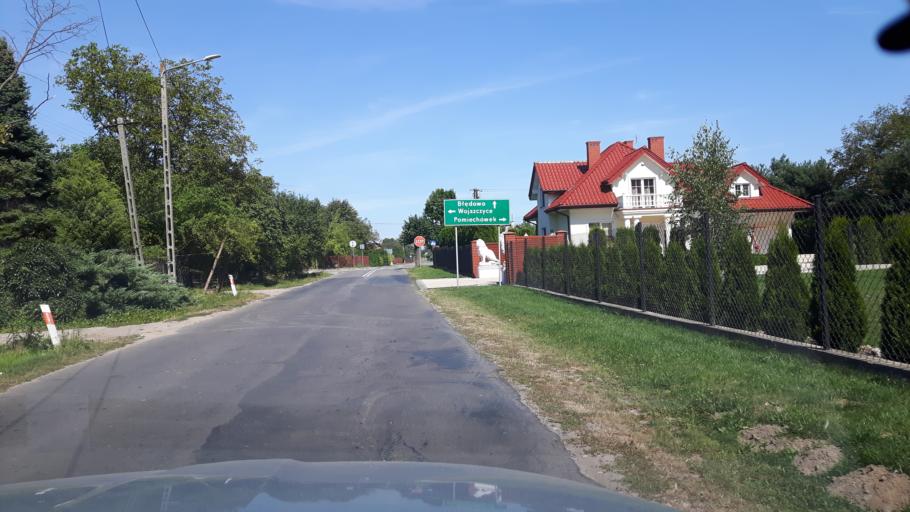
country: PL
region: Masovian Voivodeship
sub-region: Powiat nowodworski
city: Zakroczym
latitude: 52.4893
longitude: 20.6249
